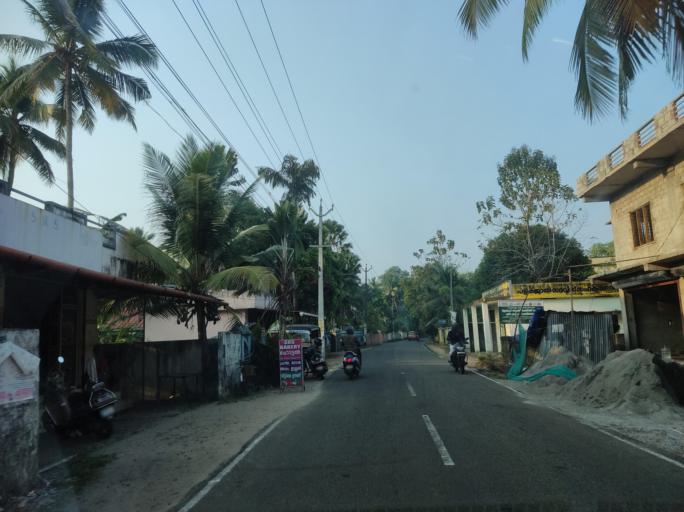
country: IN
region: Kerala
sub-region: Alappuzha
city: Shertallai
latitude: 9.6107
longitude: 76.3129
